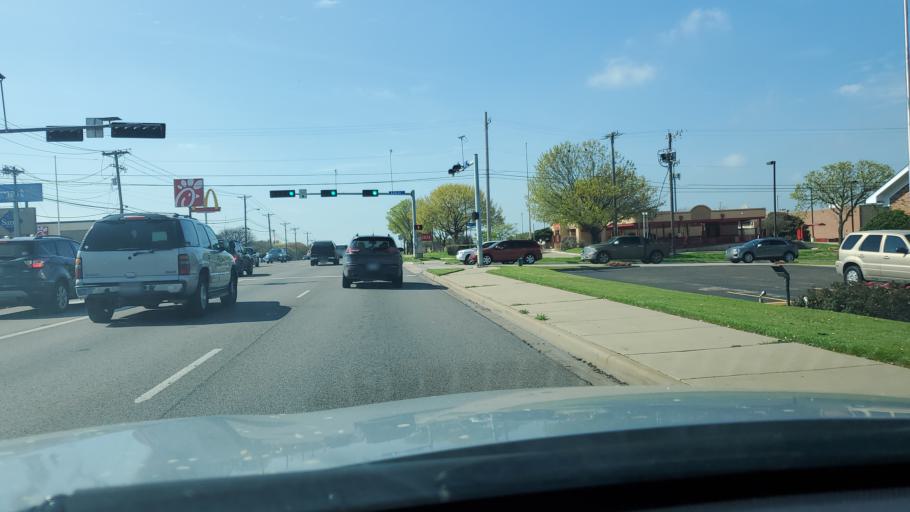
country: US
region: Texas
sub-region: Bell County
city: Temple
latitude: 31.0693
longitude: -97.3696
